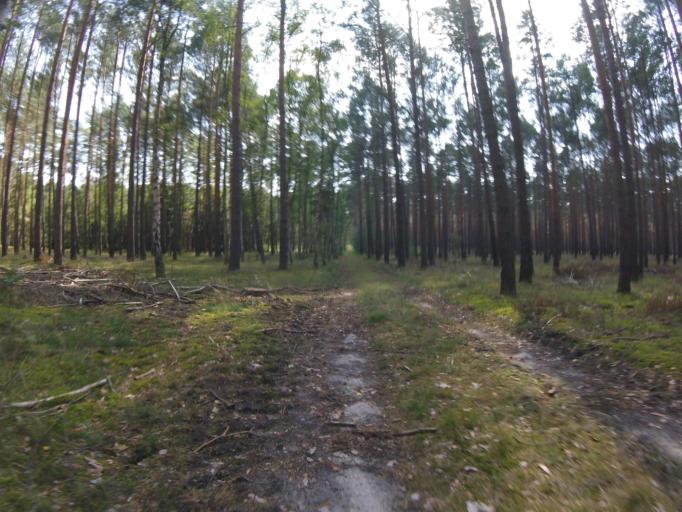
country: DE
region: Brandenburg
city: Gross Koris
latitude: 52.2092
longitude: 13.6957
